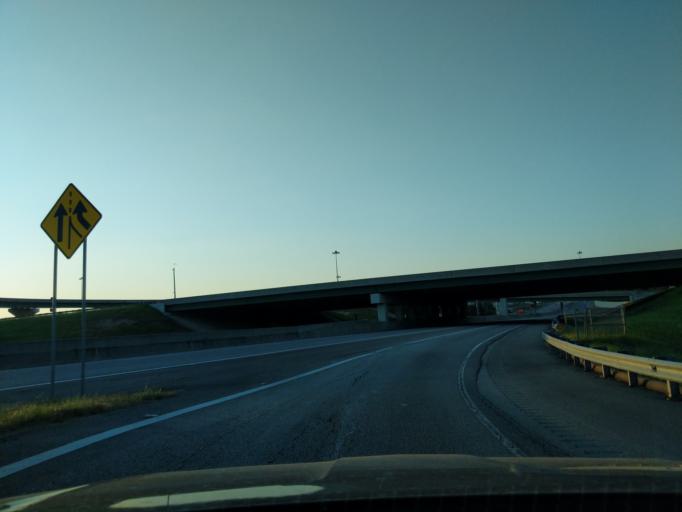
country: US
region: Georgia
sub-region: Columbia County
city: Martinez
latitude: 33.4924
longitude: -82.0836
